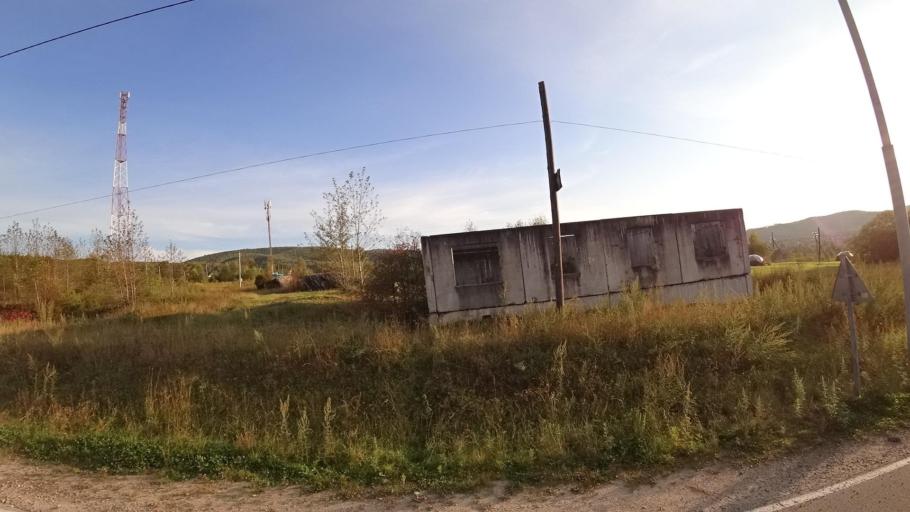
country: RU
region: Jewish Autonomous Oblast
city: Kul'dur
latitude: 49.2040
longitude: 131.6400
